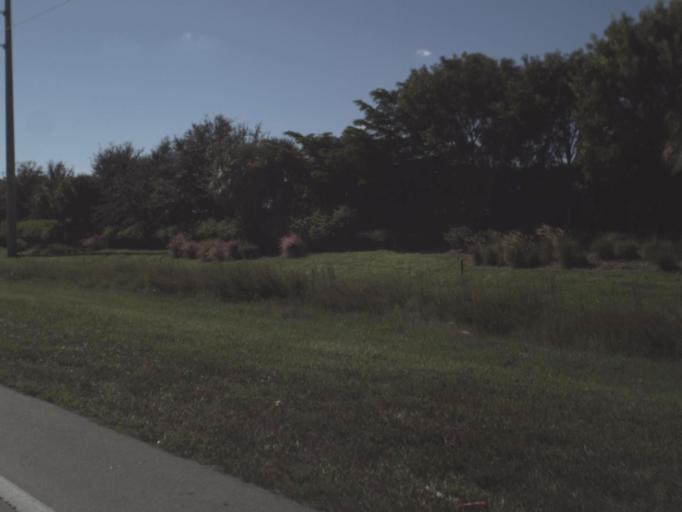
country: US
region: Florida
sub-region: Lee County
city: Gateway
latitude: 26.6069
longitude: -81.7544
